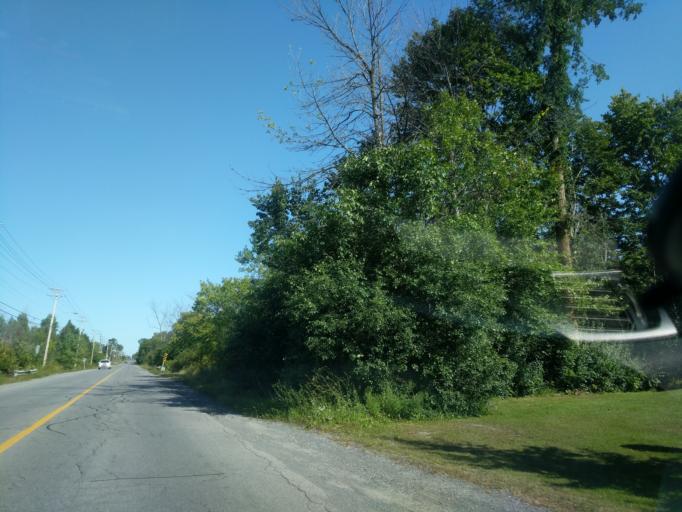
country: CA
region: Ontario
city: Bells Corners
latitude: 45.4115
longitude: -75.8197
